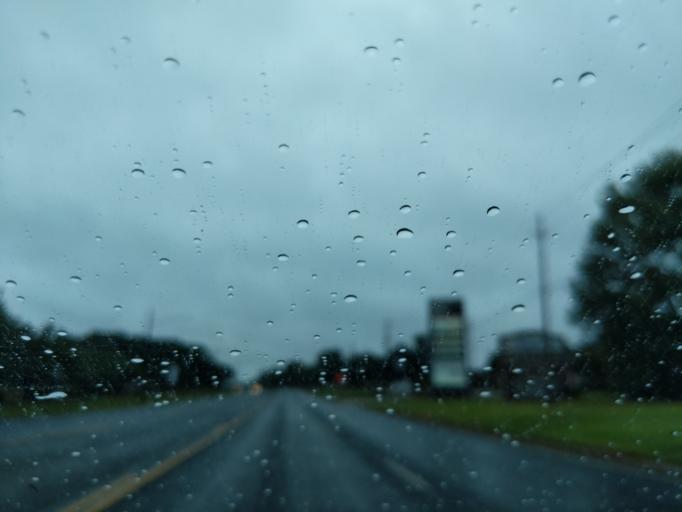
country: US
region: Texas
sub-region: Nacogdoches County
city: Nacogdoches
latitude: 31.6540
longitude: -94.6564
